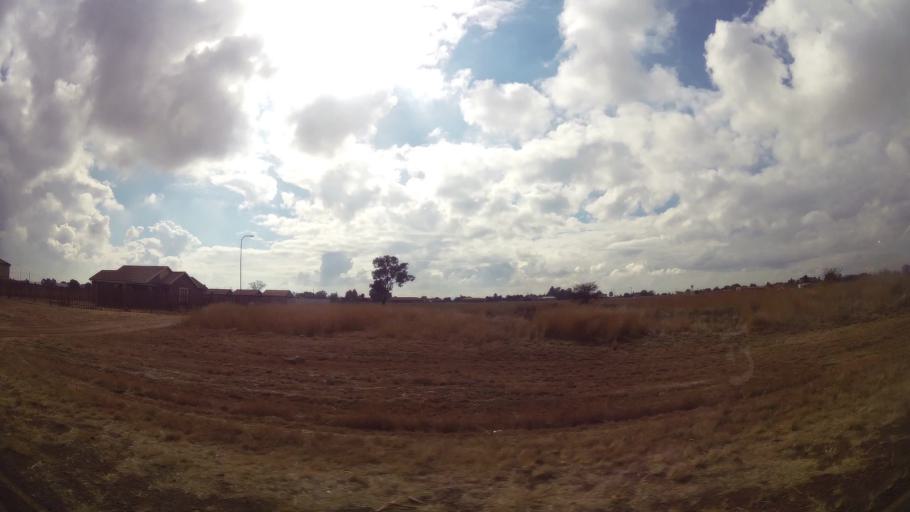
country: ZA
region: Gauteng
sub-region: Sedibeng District Municipality
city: Meyerton
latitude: -26.6129
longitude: 28.0501
